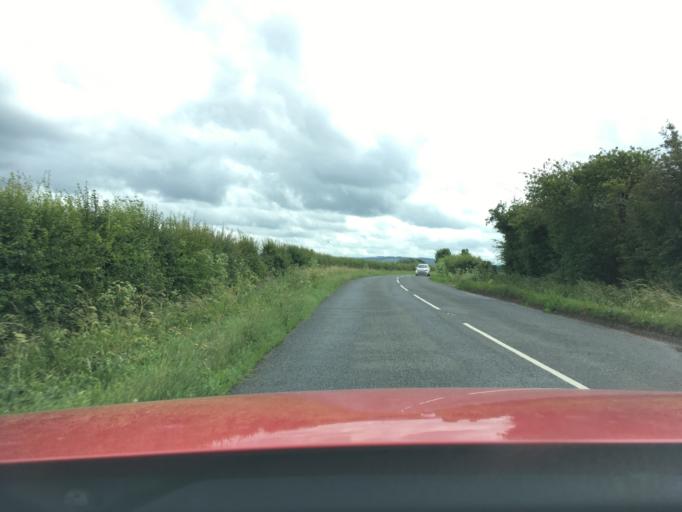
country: GB
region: England
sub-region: Worcestershire
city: Evesham
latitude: 52.0381
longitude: -1.9629
